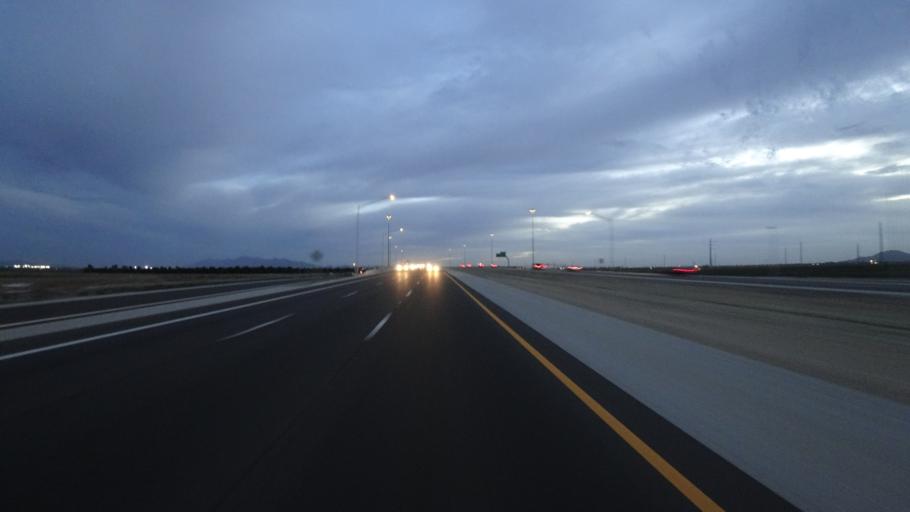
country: US
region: Arizona
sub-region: Maricopa County
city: Citrus Park
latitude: 33.5260
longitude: -112.4184
